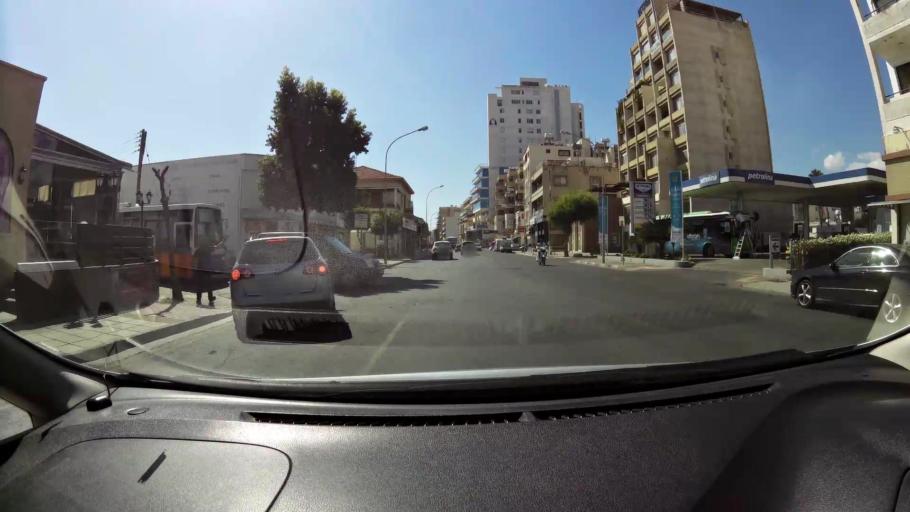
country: CY
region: Larnaka
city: Larnaca
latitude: 34.9198
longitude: 33.6368
